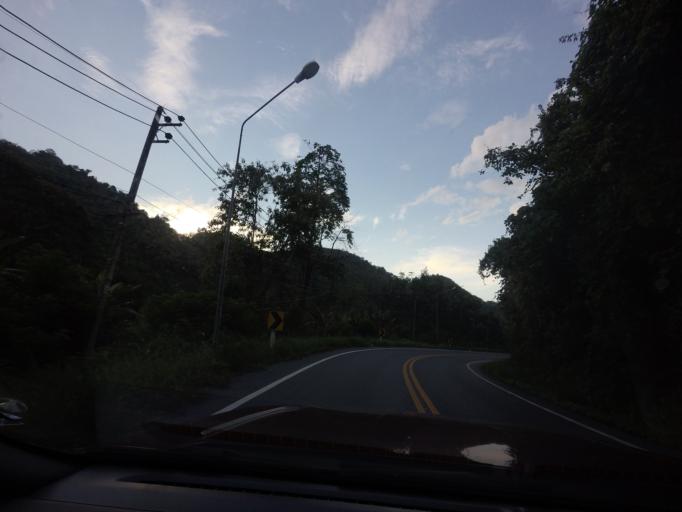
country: TH
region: Yala
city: Than To
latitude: 6.0361
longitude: 101.1984
